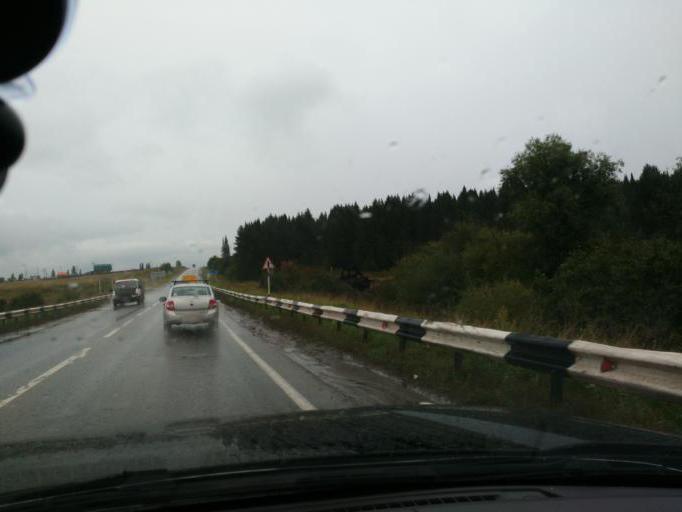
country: RU
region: Perm
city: Yugo-Kamskiy
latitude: 57.6886
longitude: 55.5697
